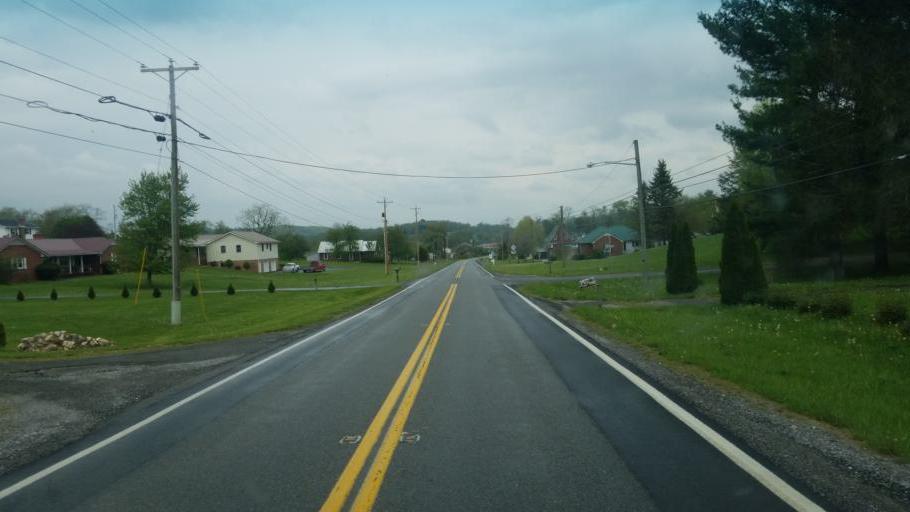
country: US
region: Virginia
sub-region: Wythe County
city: Rural Retreat
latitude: 36.9085
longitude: -81.2832
